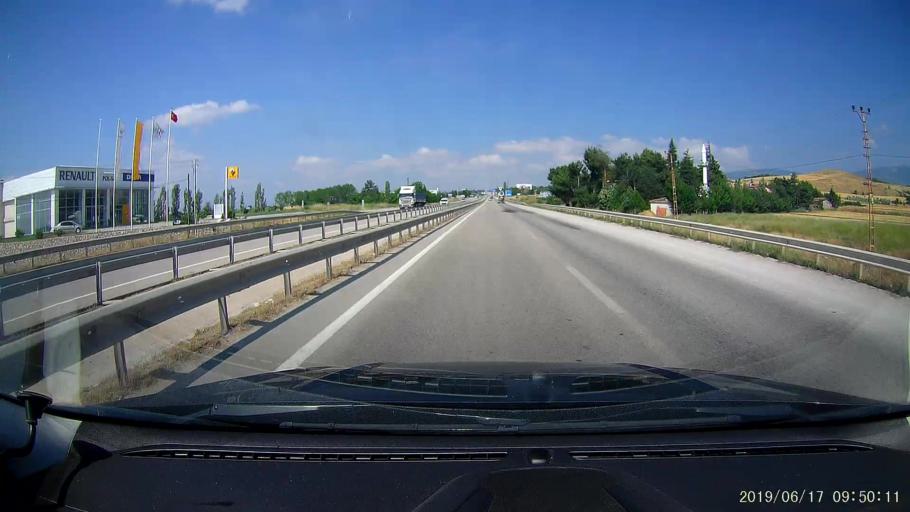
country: TR
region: Amasya
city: Merzifon
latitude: 40.8714
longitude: 35.5132
